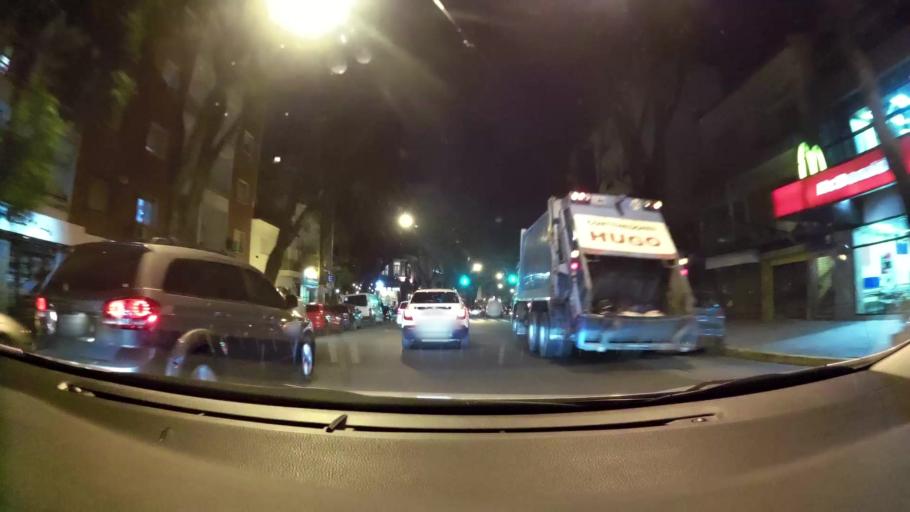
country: AR
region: Buenos Aires F.D.
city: Colegiales
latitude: -34.5737
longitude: -58.4597
